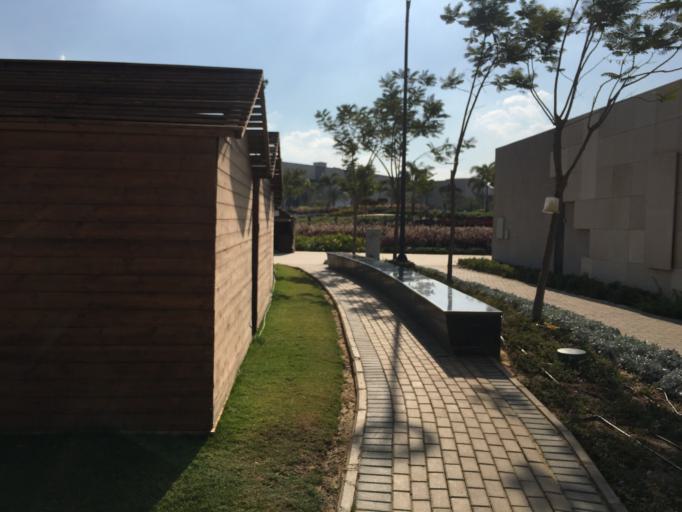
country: EG
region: Al Jizah
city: Awsim
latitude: 30.0089
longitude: 30.9773
